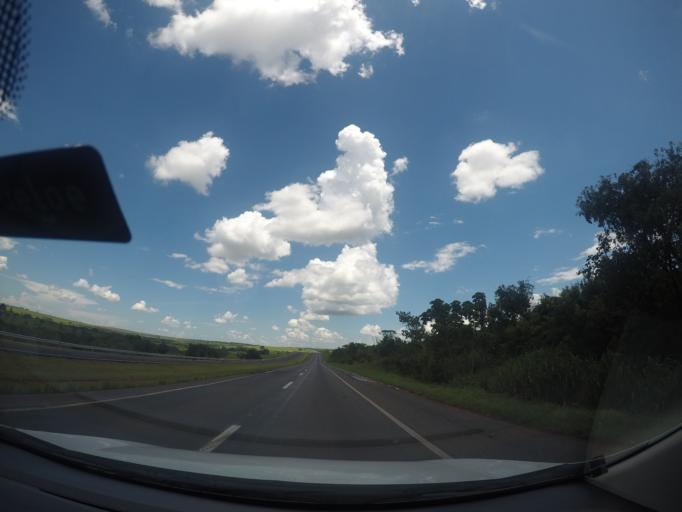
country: BR
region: Minas Gerais
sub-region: Prata
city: Prata
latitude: -19.4244
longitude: -48.8892
